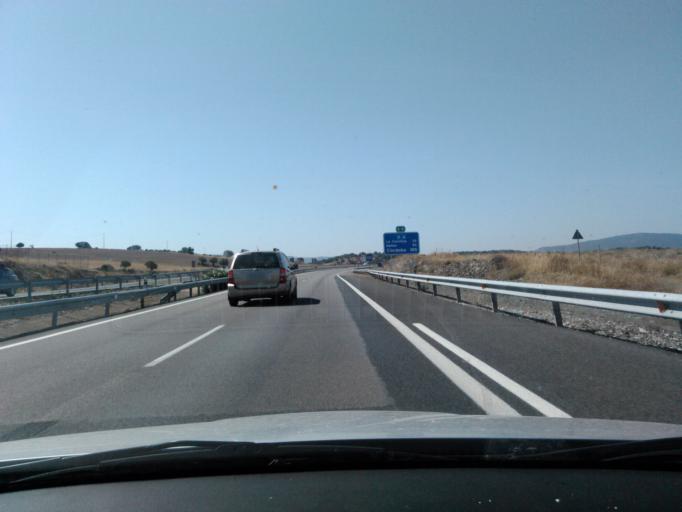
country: ES
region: Castille-La Mancha
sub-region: Provincia de Ciudad Real
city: Viso del Marques
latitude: 38.4894
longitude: -3.5020
